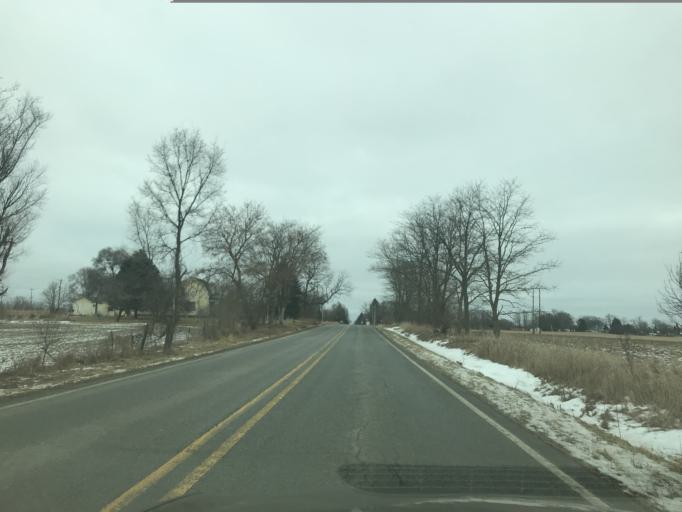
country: US
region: Michigan
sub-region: Jackson County
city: Brooklyn
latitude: 42.0734
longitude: -84.3389
